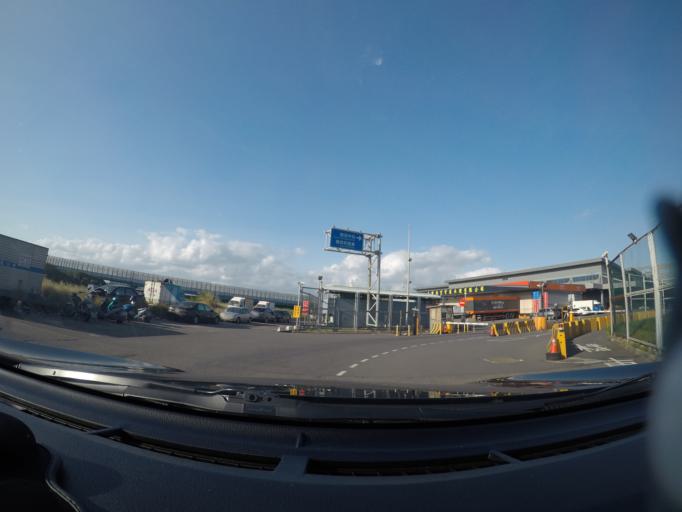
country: TW
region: Taiwan
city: Taoyuan City
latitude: 25.0967
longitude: 121.2515
